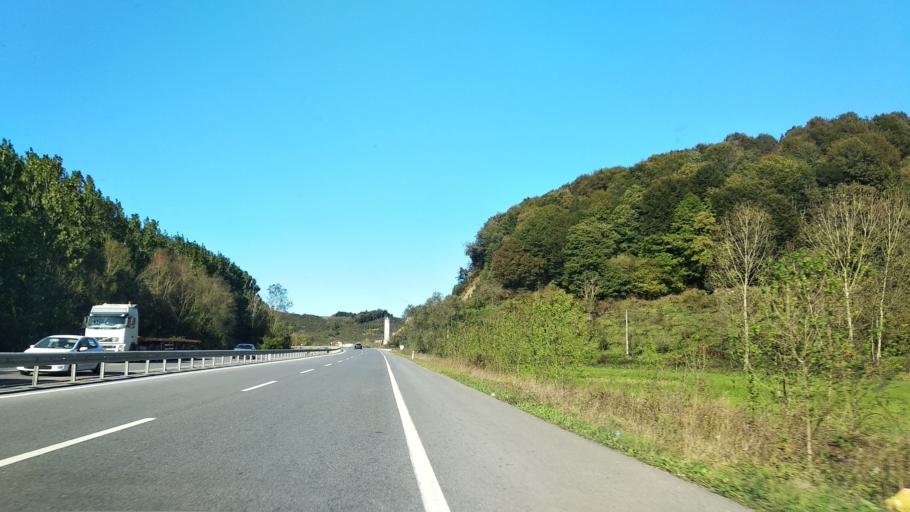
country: TR
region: Sakarya
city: Karasu
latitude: 41.0713
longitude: 30.6455
